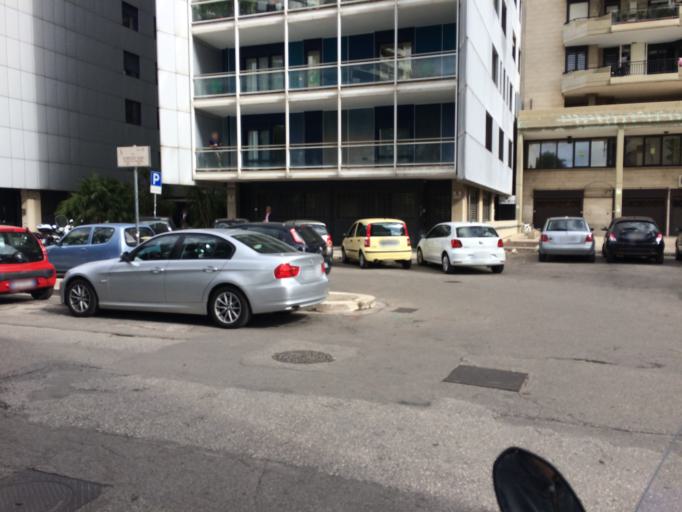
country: IT
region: Apulia
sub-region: Provincia di Bari
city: Bari
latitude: 41.0991
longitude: 16.8533
